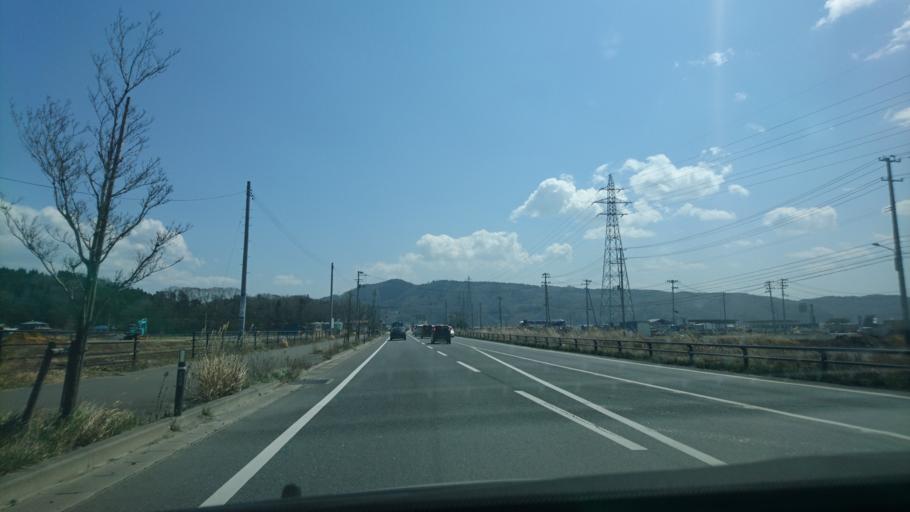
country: JP
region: Miyagi
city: Ishinomaki
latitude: 38.4533
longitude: 141.3113
